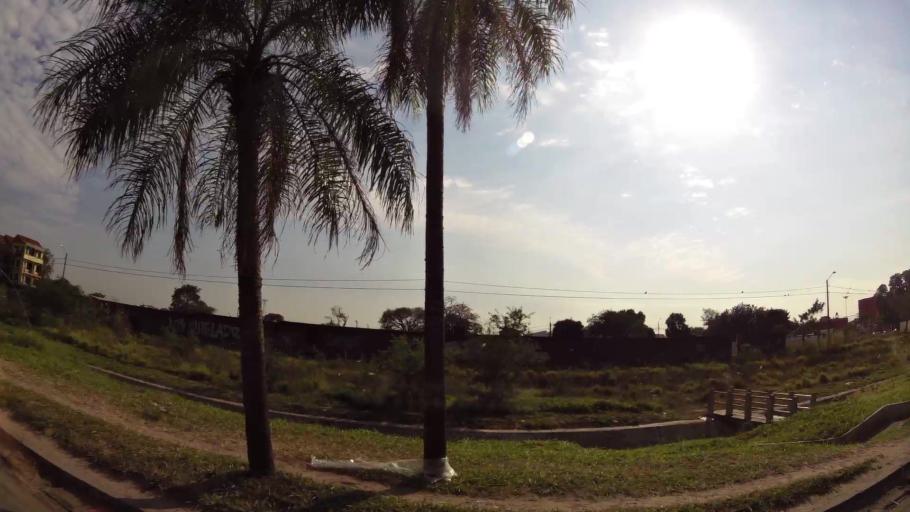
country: BO
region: Santa Cruz
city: Santa Cruz de la Sierra
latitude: -17.7301
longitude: -63.1741
